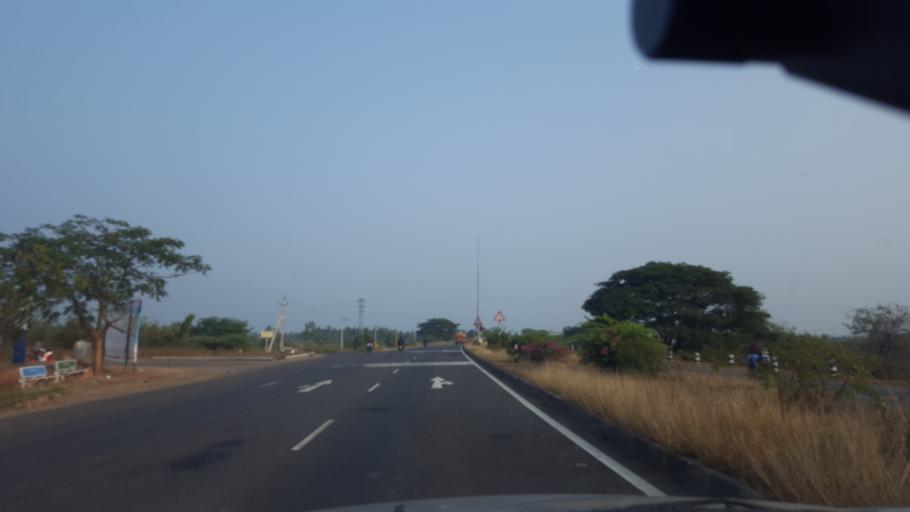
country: IN
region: Andhra Pradesh
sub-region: West Godavari
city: Tadepallegudem
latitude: 16.8412
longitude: 81.5346
